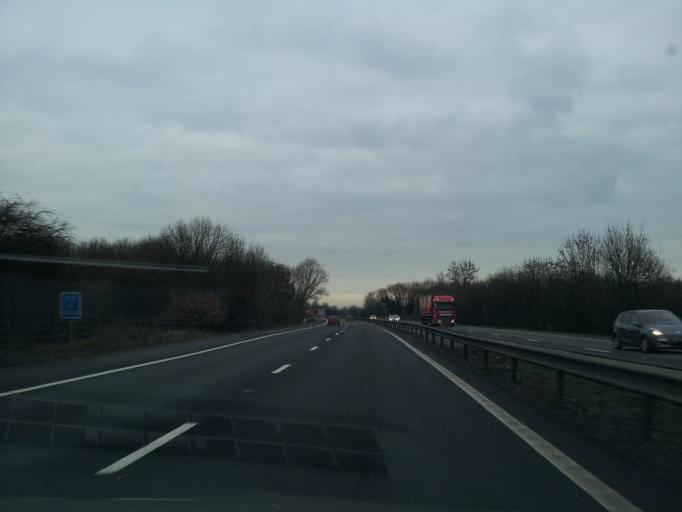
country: GB
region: England
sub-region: Cambridgeshire
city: Girton
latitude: 52.2166
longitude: 0.0786
